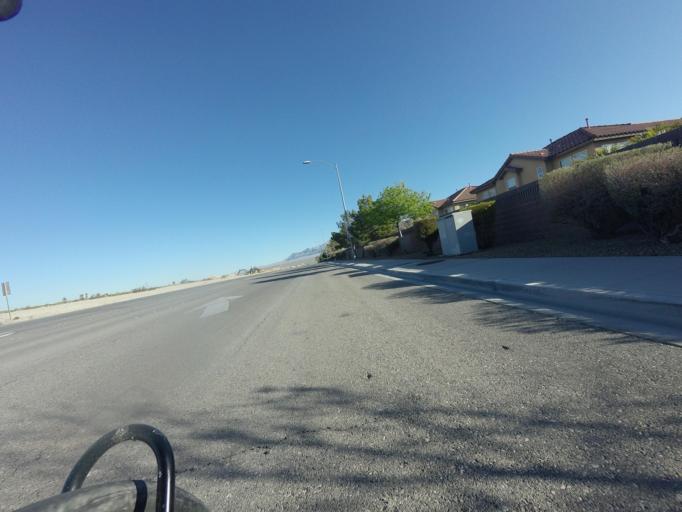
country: US
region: Nevada
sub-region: Clark County
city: Summerlin South
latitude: 36.3216
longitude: -115.2966
